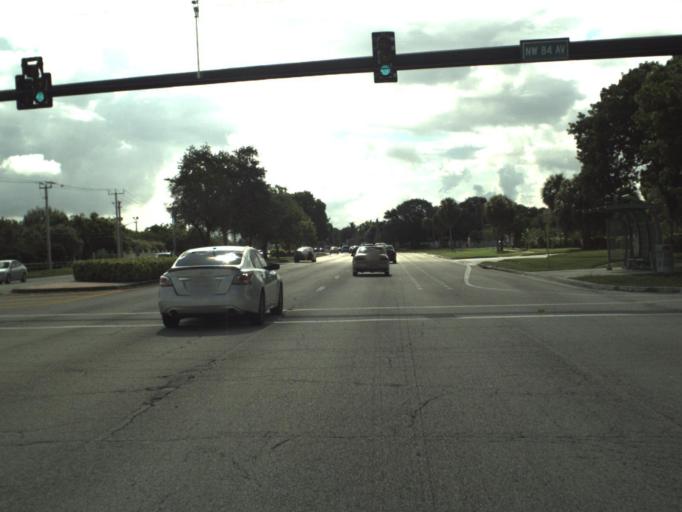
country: US
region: Florida
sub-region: Broward County
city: Plantation
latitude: 26.1674
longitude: -80.2622
